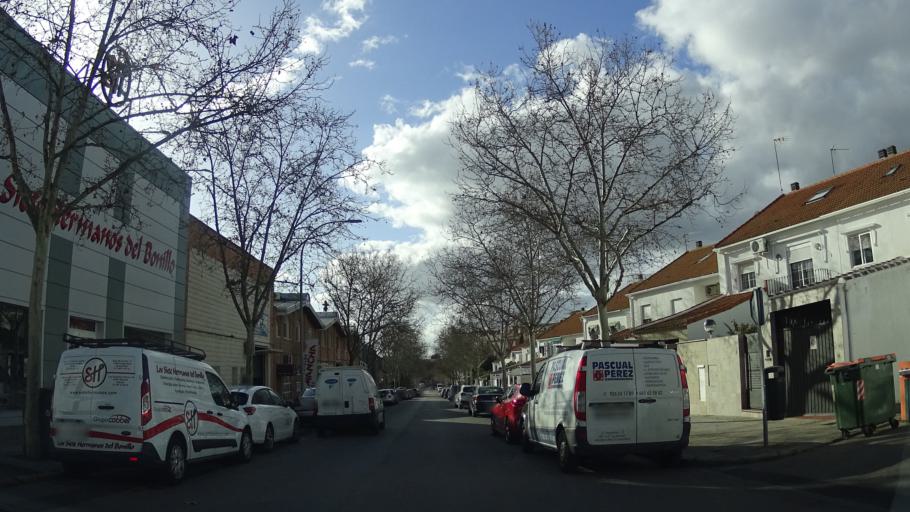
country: ES
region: Castille-La Mancha
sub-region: Provincia de Ciudad Real
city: Ciudad Real
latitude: 38.9779
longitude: -3.9317
